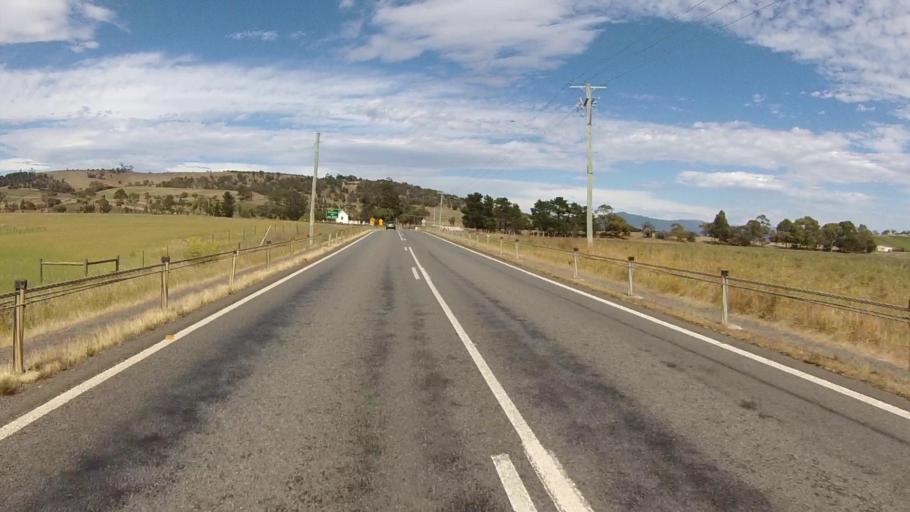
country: AU
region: Tasmania
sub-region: Brighton
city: Old Beach
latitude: -42.6900
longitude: 147.3474
